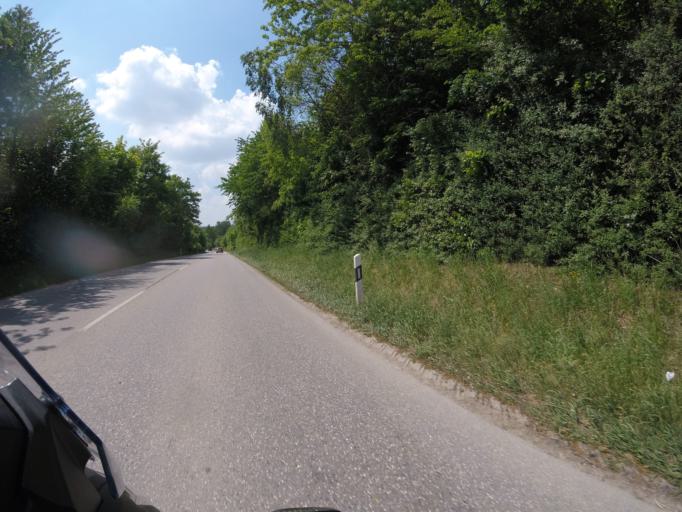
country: DE
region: Bavaria
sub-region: Upper Bavaria
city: Pfaffenhofen an der Ilm
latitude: 48.5401
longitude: 11.4928
